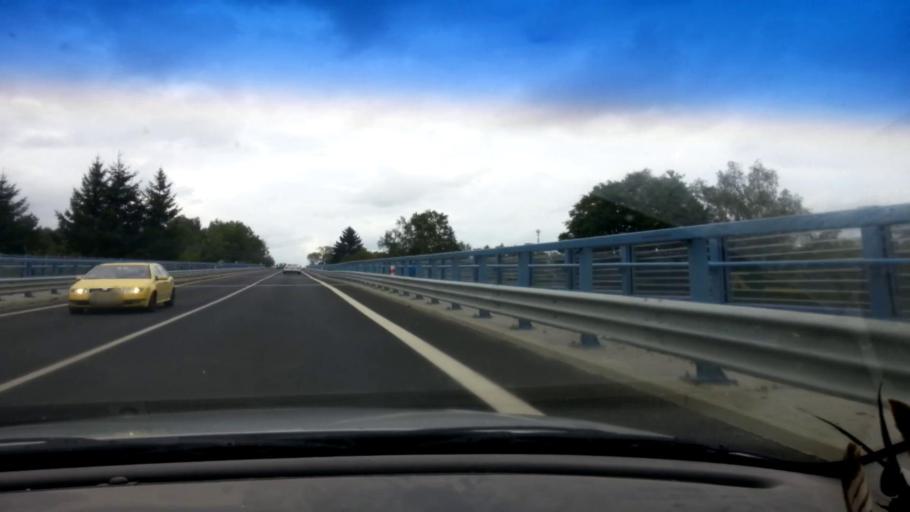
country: CZ
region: Karlovarsky
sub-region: Okres Cheb
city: Cheb
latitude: 50.0598
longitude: 12.3818
